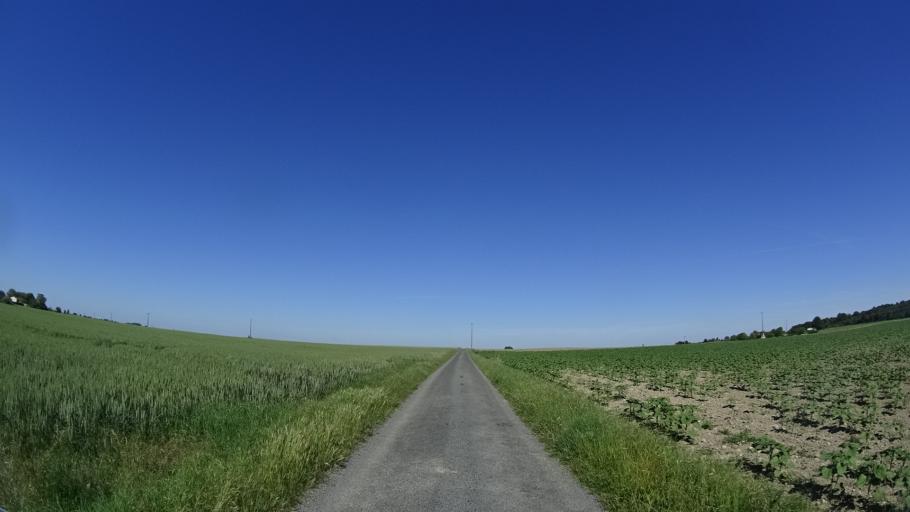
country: FR
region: Pays de la Loire
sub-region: Departement de Maine-et-Loire
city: Doue-la-Fontaine
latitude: 47.2495
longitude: -0.2772
